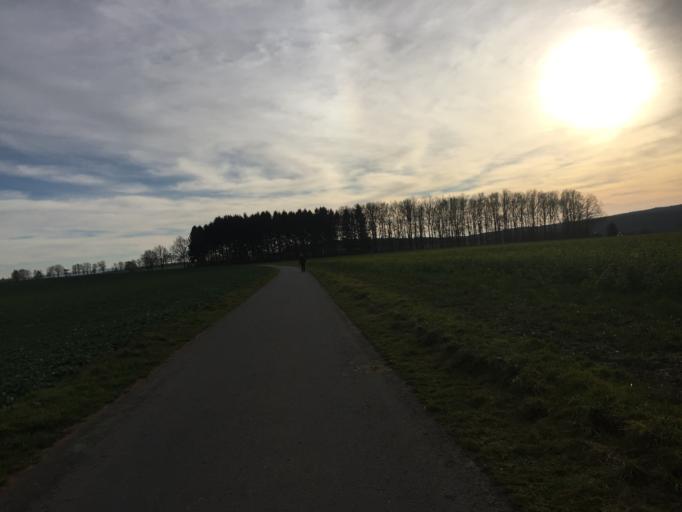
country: DE
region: Hesse
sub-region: Regierungsbezirk Darmstadt
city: Erbach
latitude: 49.6822
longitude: 8.9369
